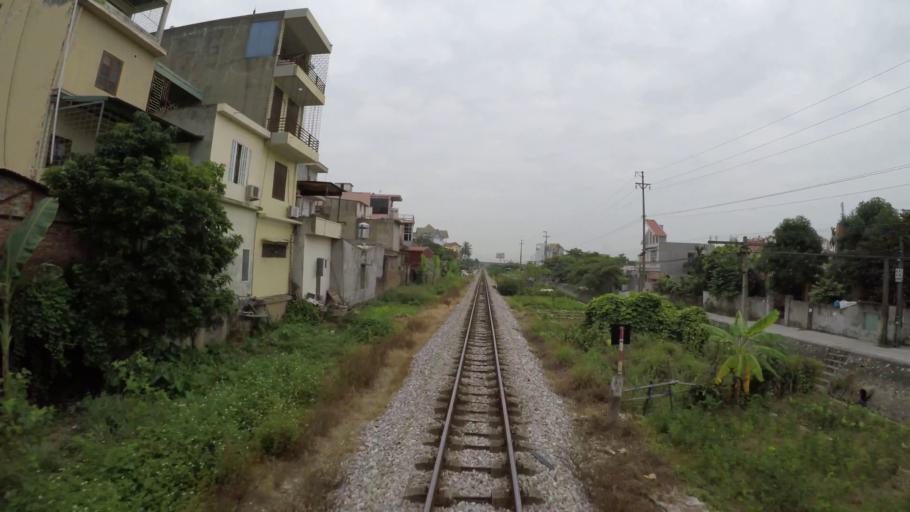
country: VN
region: Hai Phong
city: An Duong
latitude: 20.9142
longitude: 106.5660
